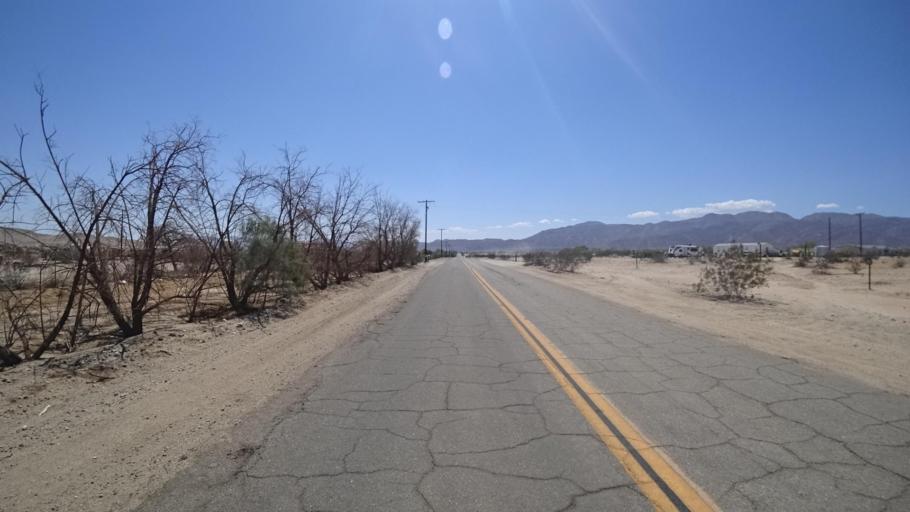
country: US
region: California
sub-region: Imperial County
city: Salton City
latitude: 33.1424
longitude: -116.1328
